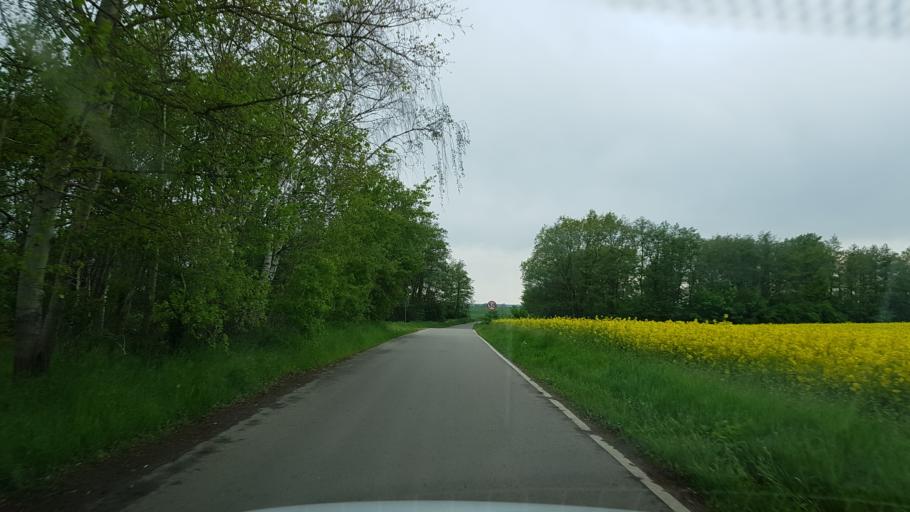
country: PL
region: West Pomeranian Voivodeship
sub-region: Powiat pyrzycki
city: Kozielice
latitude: 53.1220
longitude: 14.7570
